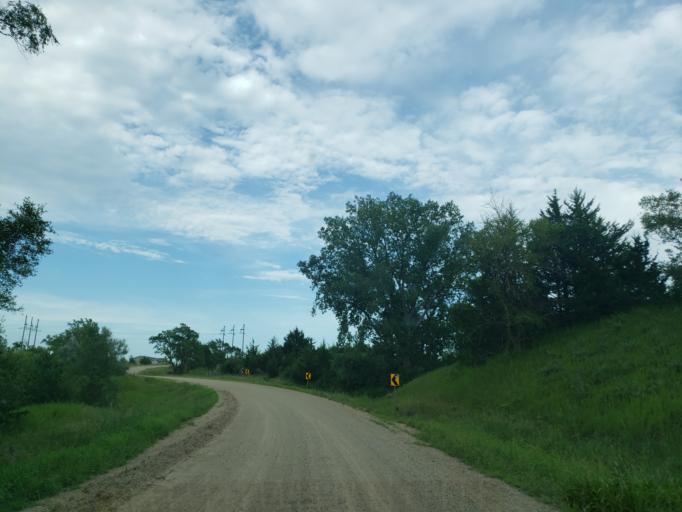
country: US
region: South Dakota
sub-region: Davison County
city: Mitchell
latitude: 43.6873
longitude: -97.9792
